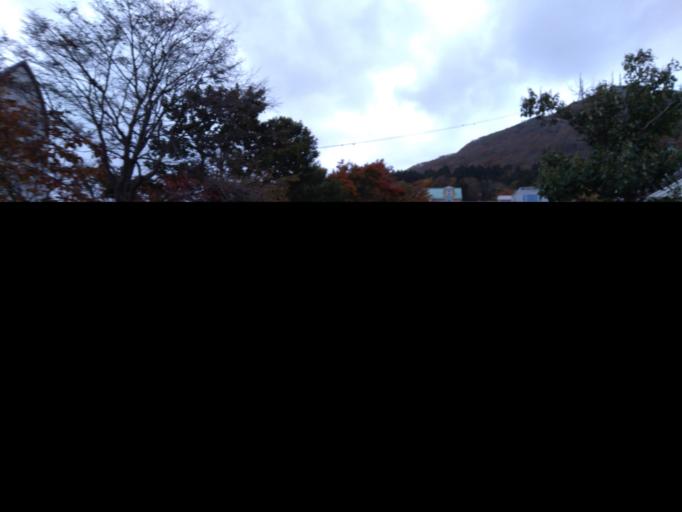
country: JP
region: Hokkaido
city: Hakodate
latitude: 41.7630
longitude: 140.7127
